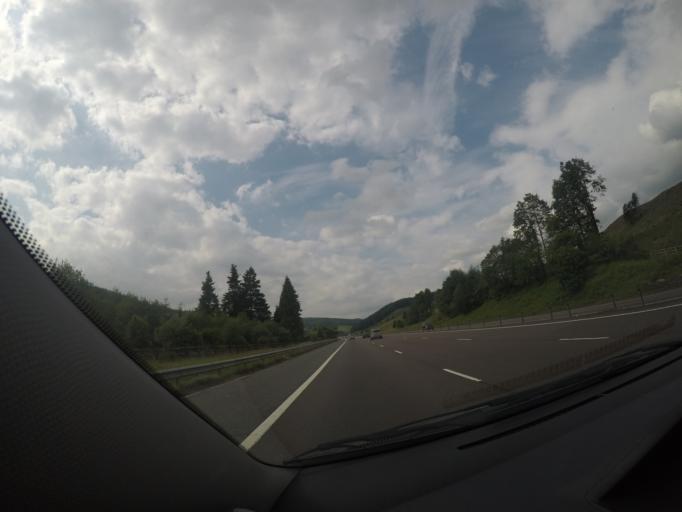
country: GB
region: Scotland
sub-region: Dumfries and Galloway
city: Moffat
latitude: 55.3517
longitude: -3.5073
